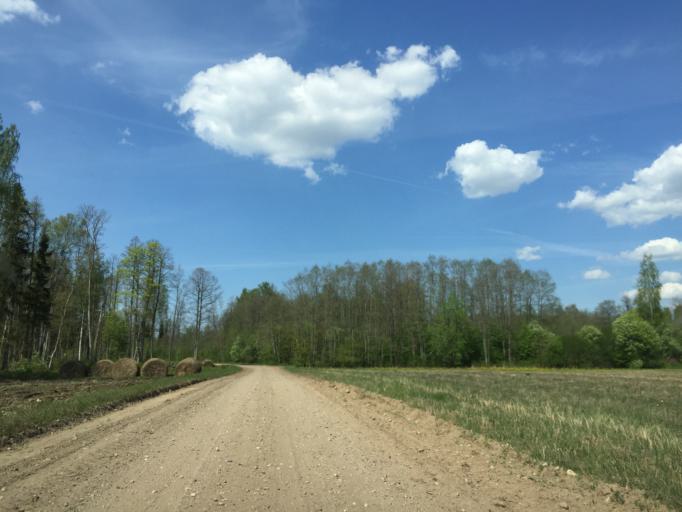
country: LV
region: Limbazu Rajons
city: Limbazi
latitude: 57.3867
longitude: 24.6032
